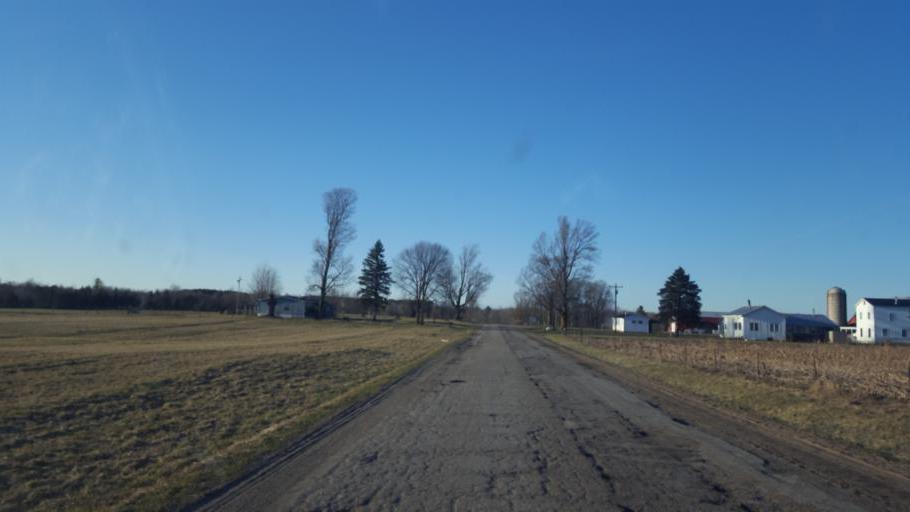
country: US
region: Michigan
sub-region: Mecosta County
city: Canadian Lakes
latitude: 43.5510
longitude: -85.3928
